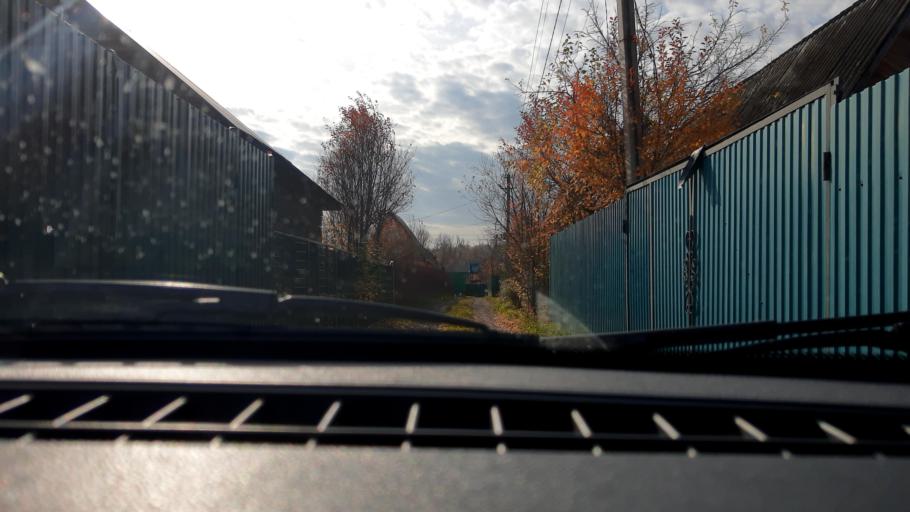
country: RU
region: Bashkortostan
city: Ufa
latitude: 54.6012
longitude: 55.8956
